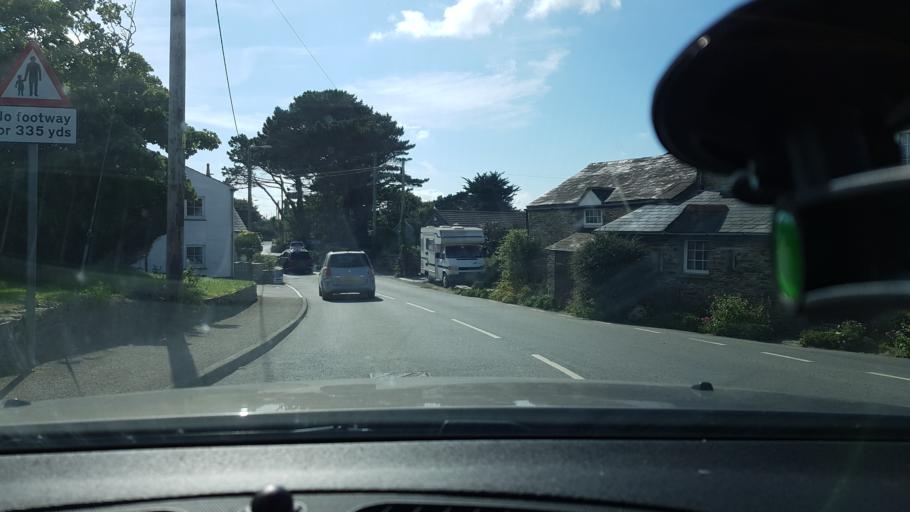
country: GB
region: England
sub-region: Cornwall
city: Tintagel
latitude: 50.6683
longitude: -4.7357
